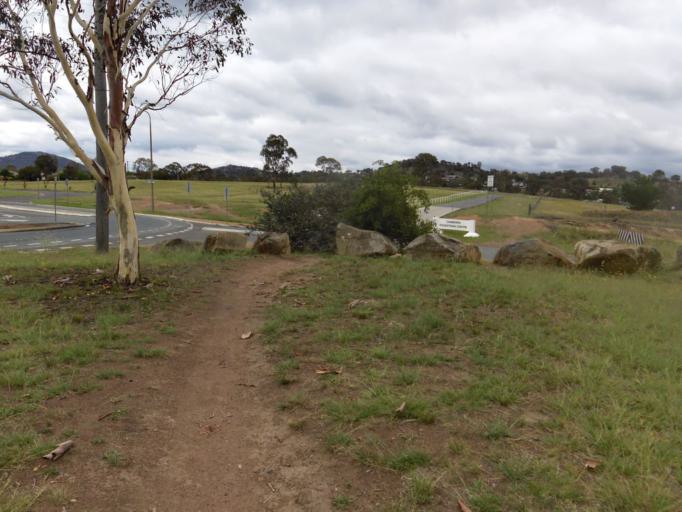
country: AU
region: Australian Capital Territory
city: Macquarie
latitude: -35.3436
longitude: 149.0266
